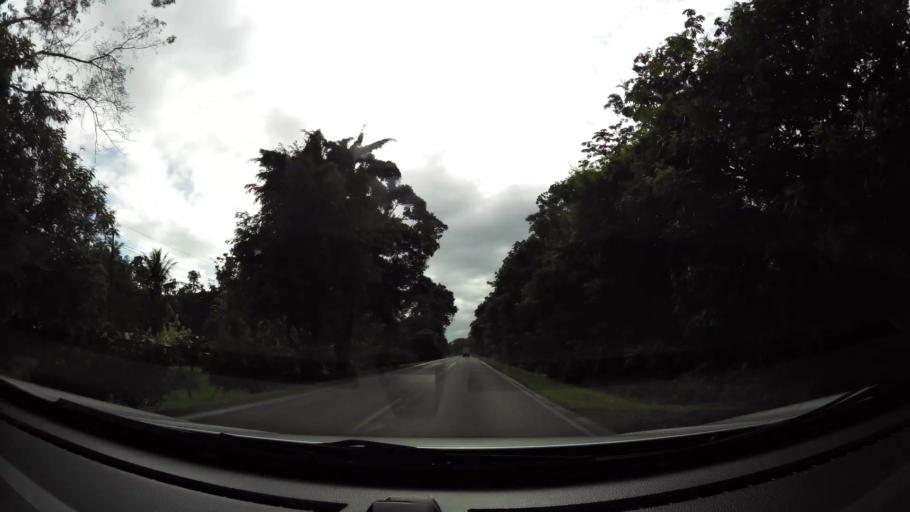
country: CR
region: Limon
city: Pocora
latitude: 10.1847
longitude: -83.6295
